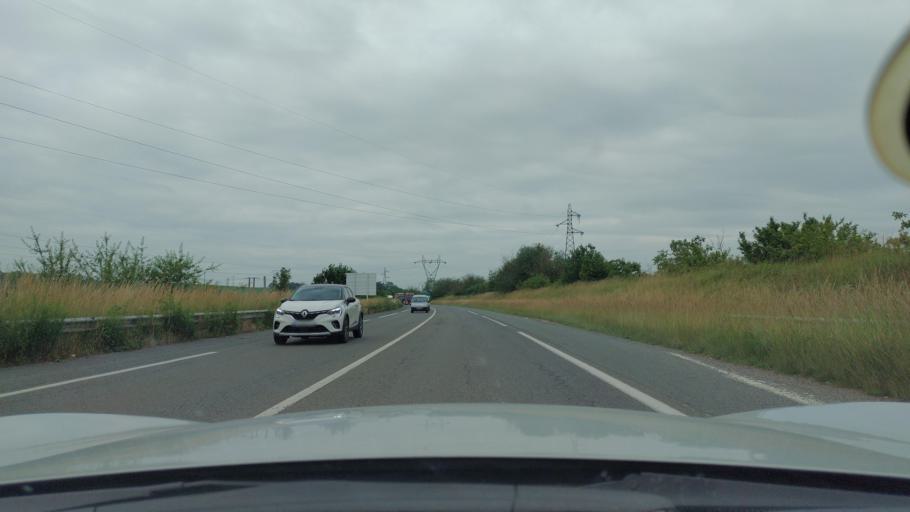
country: FR
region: Picardie
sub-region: Departement de l'Oise
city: Clairoix
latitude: 49.4379
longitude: 2.8404
